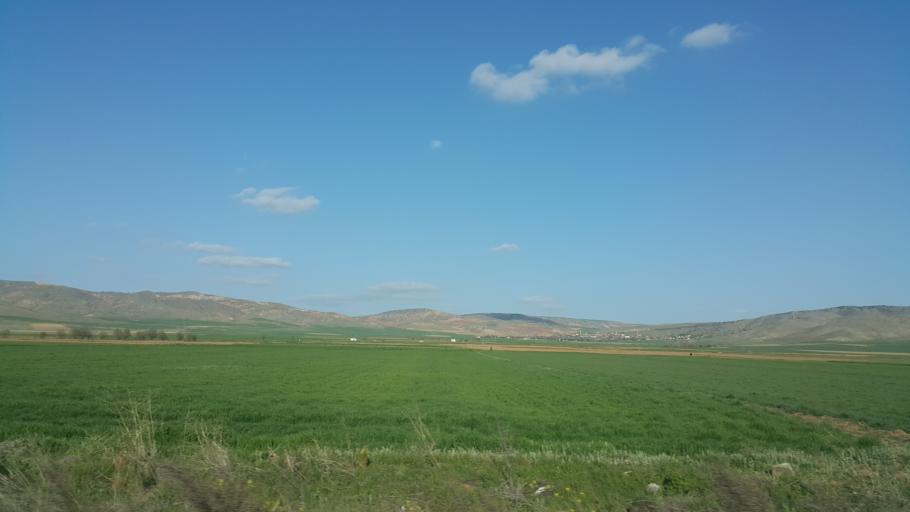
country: TR
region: Ankara
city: Sereflikochisar
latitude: 38.8618
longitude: 33.5890
